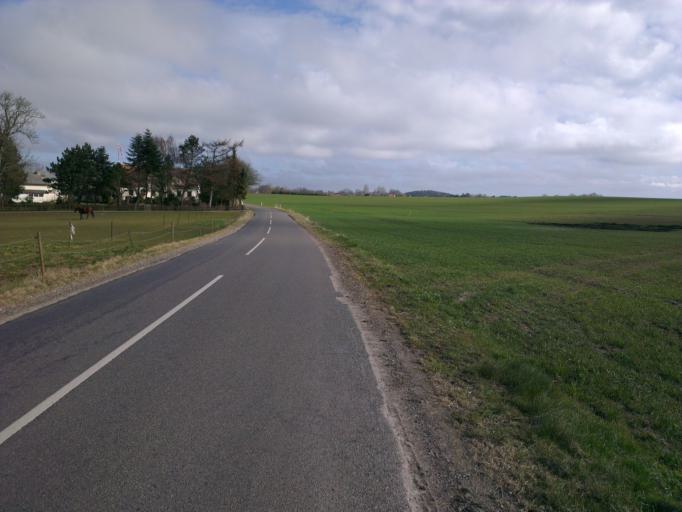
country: DK
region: Capital Region
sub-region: Hillerod Kommune
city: Skaevinge
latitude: 55.8756
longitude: 12.1202
